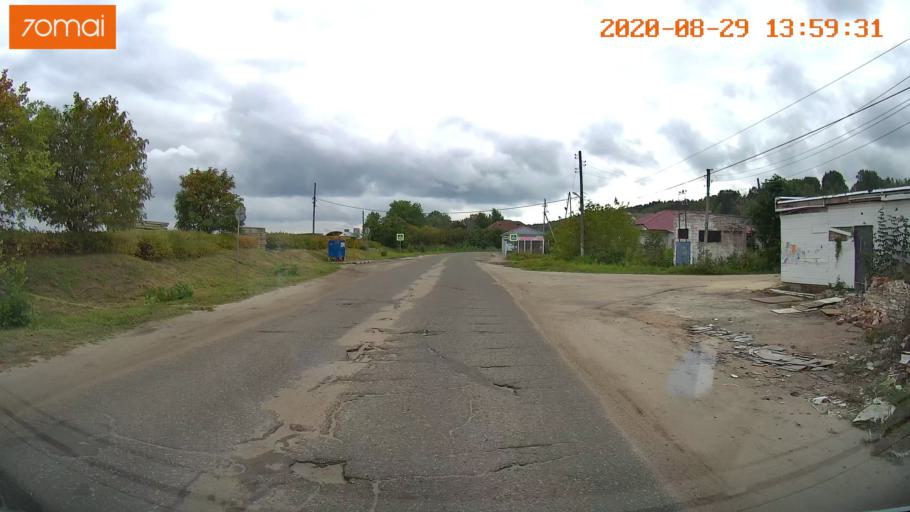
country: RU
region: Ivanovo
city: Yur'yevets
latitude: 57.3156
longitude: 43.1115
